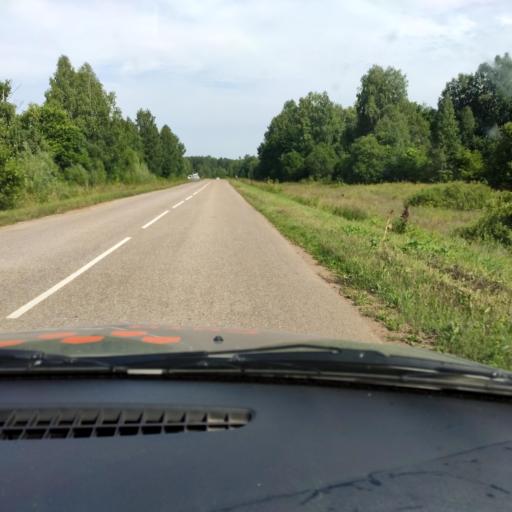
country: RU
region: Bashkortostan
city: Pavlovka
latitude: 55.3856
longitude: 56.4971
